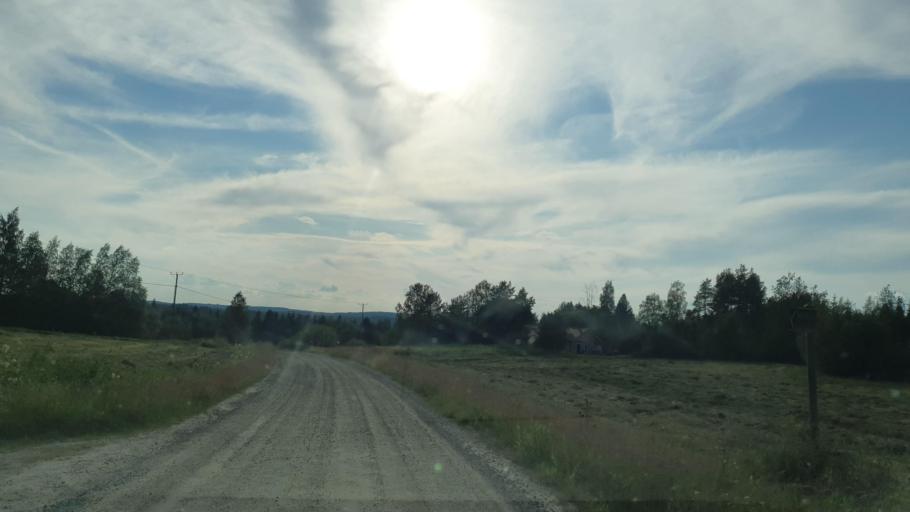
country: FI
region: Kainuu
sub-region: Kehys-Kainuu
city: Kuhmo
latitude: 64.2449
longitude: 29.4937
